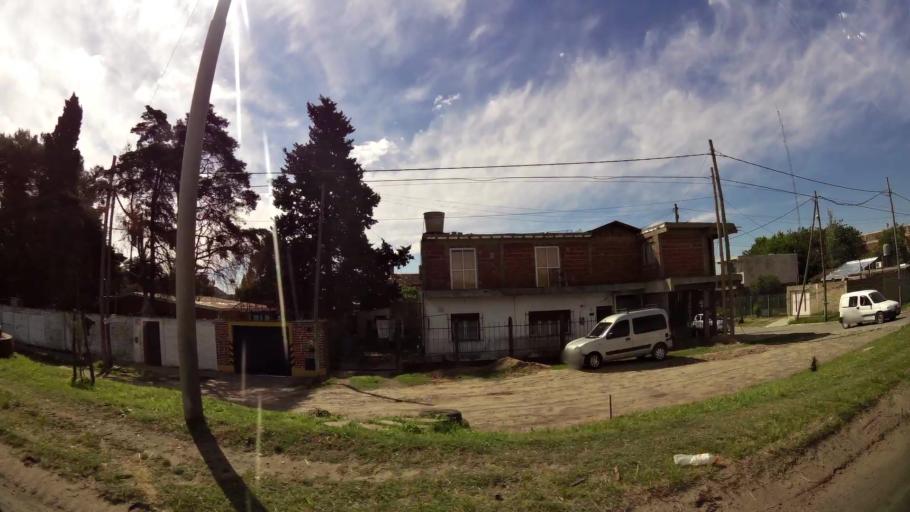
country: AR
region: Buenos Aires
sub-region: Partido de Quilmes
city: Quilmes
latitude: -34.7862
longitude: -58.3033
